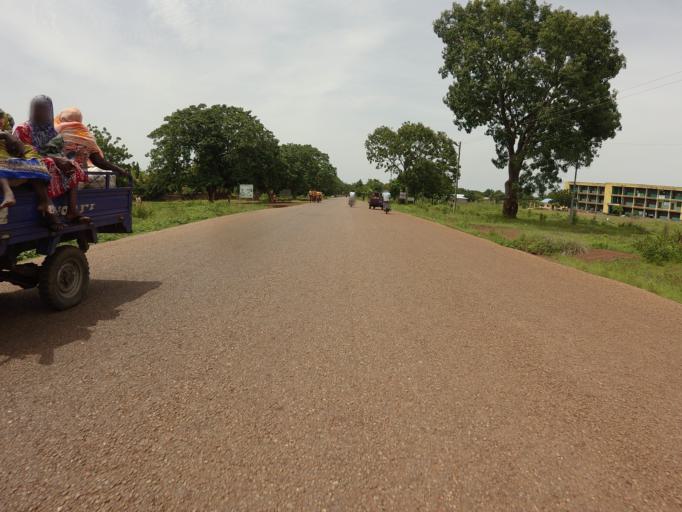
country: GH
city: Kpandae
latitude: 8.8678
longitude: 0.0491
